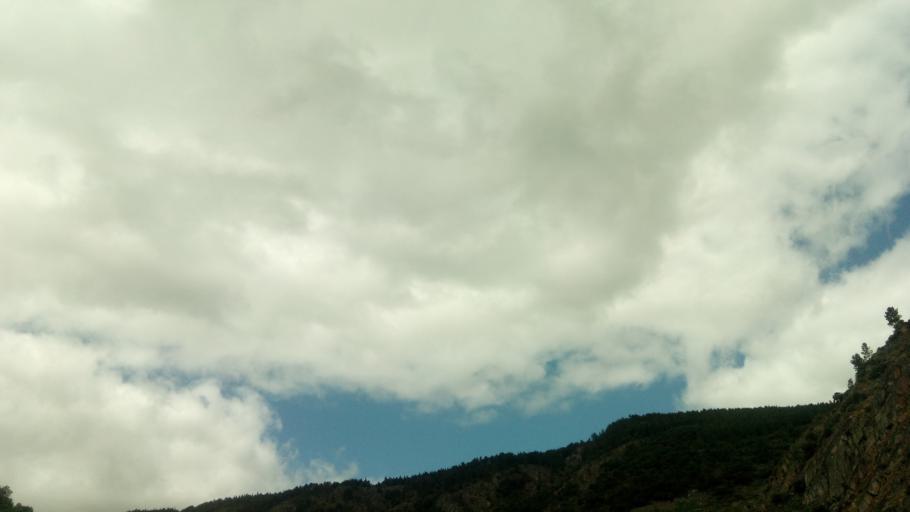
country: ES
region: Galicia
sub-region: Provincia de Lugo
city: Lobios
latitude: 42.4034
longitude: -7.5691
